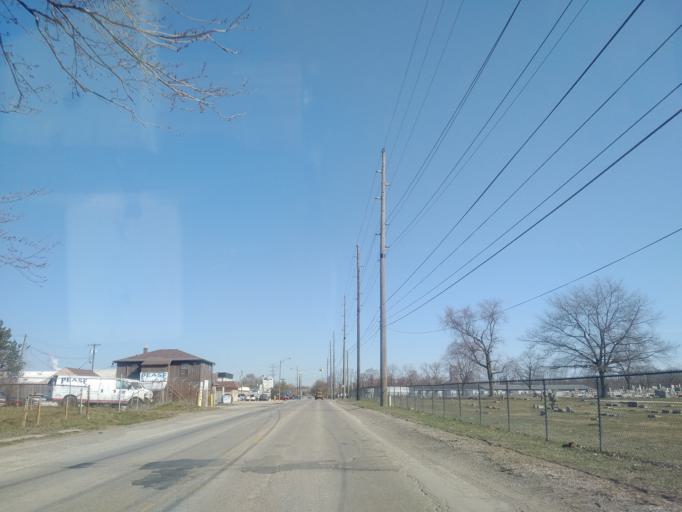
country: US
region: Indiana
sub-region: Marion County
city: Indianapolis
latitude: 39.7300
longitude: -86.1683
